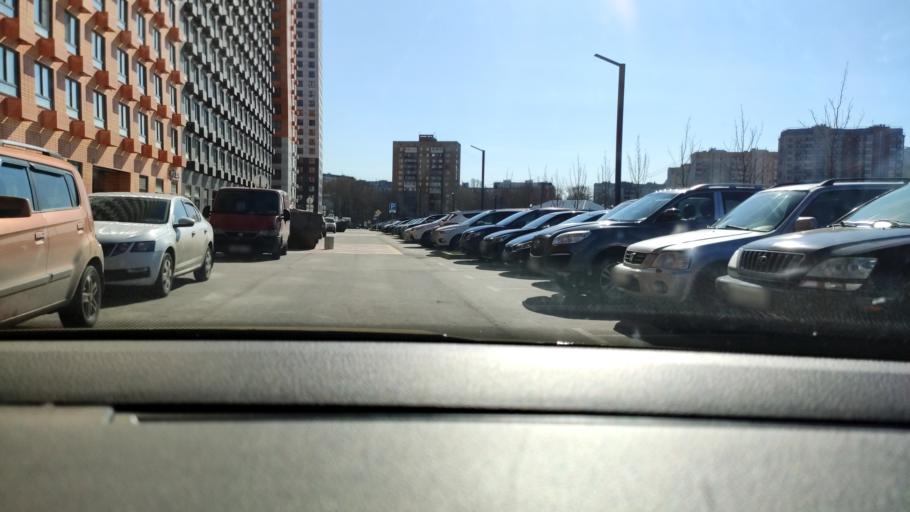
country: RU
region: Moscow
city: Kozeyevo
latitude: 55.8822
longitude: 37.6343
